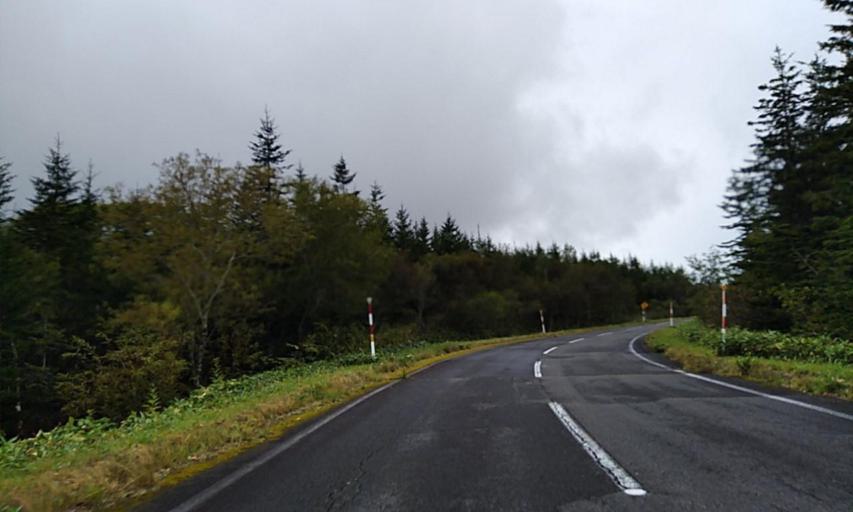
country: JP
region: Hokkaido
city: Abashiri
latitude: 43.6062
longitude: 144.5873
